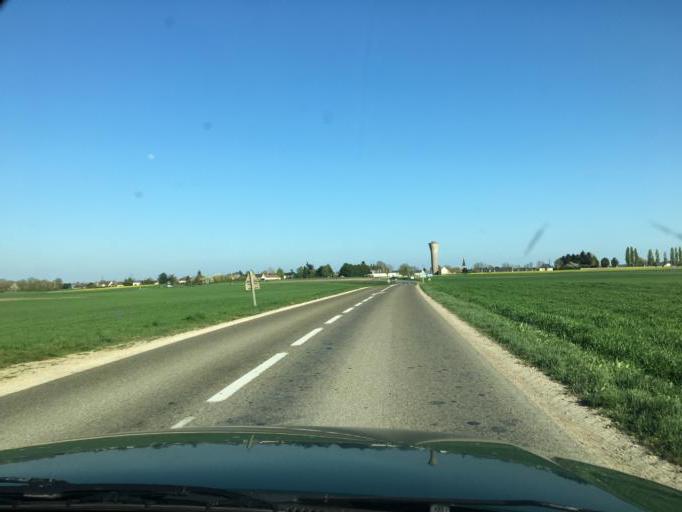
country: FR
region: Centre
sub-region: Departement du Loiret
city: Baule
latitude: 47.8468
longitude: 1.6428
